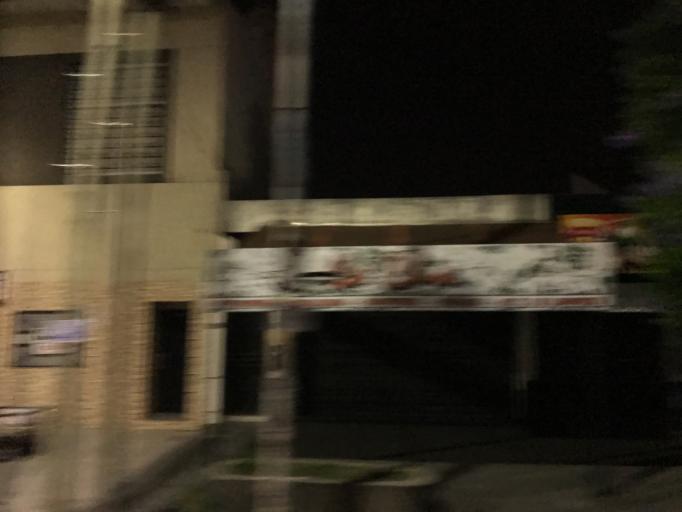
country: AR
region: Buenos Aires
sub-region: Partido de Lanus
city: Lanus
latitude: -34.6882
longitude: -58.4169
